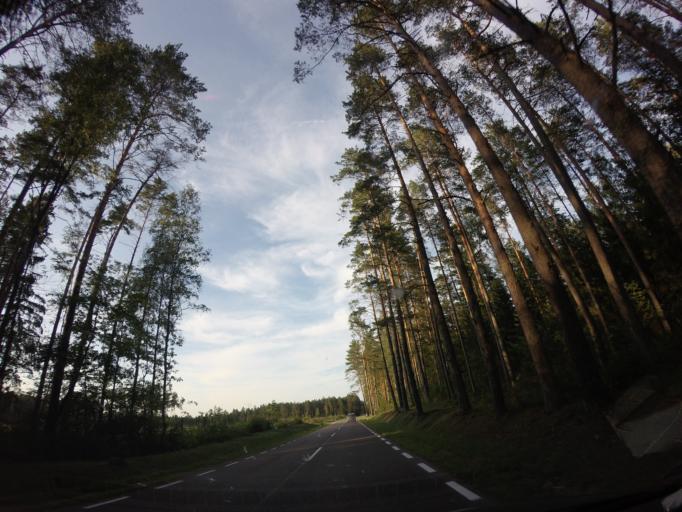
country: PL
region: Podlasie
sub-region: Powiat augustowski
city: Augustow
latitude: 53.9011
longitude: 23.1295
